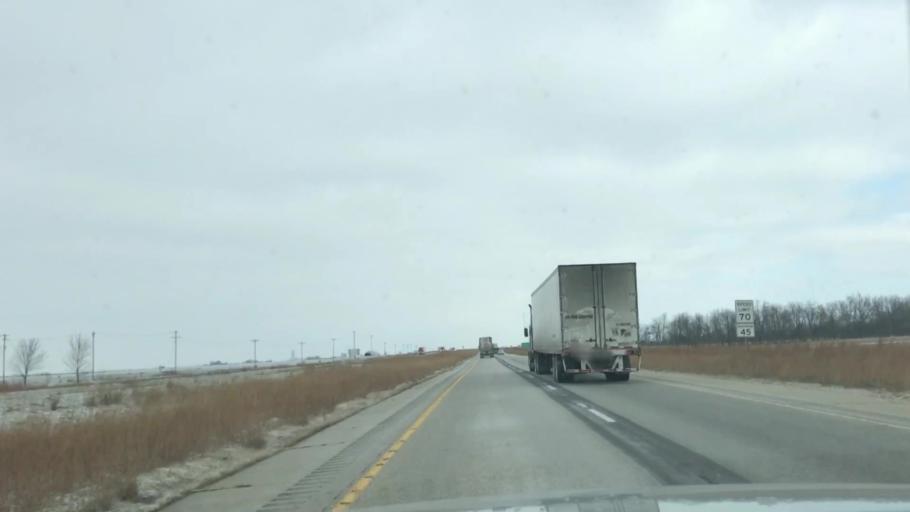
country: US
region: Illinois
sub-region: Sangamon County
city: Divernon
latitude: 39.4564
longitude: -89.6441
